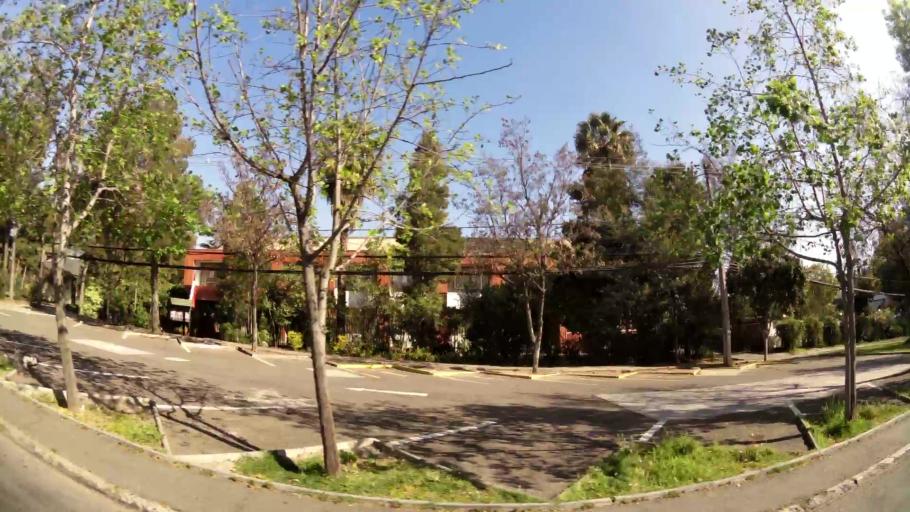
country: CL
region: Santiago Metropolitan
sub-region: Provincia de Santiago
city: Villa Presidente Frei, Nunoa, Santiago, Chile
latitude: -33.3945
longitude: -70.5275
